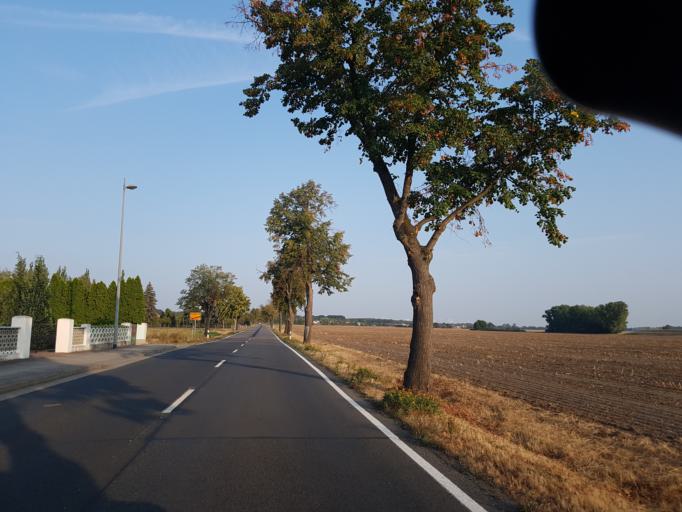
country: DE
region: Saxony-Anhalt
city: Pretzsch
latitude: 51.7200
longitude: 12.7965
